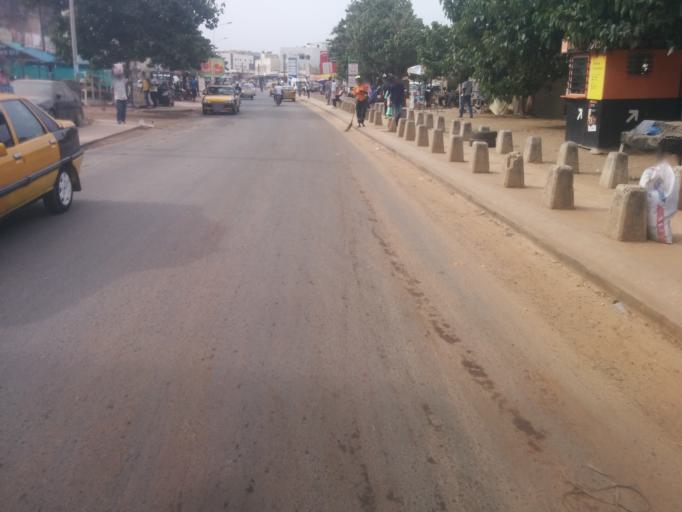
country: SN
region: Dakar
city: Grand Dakar
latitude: 14.7355
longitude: -17.4558
